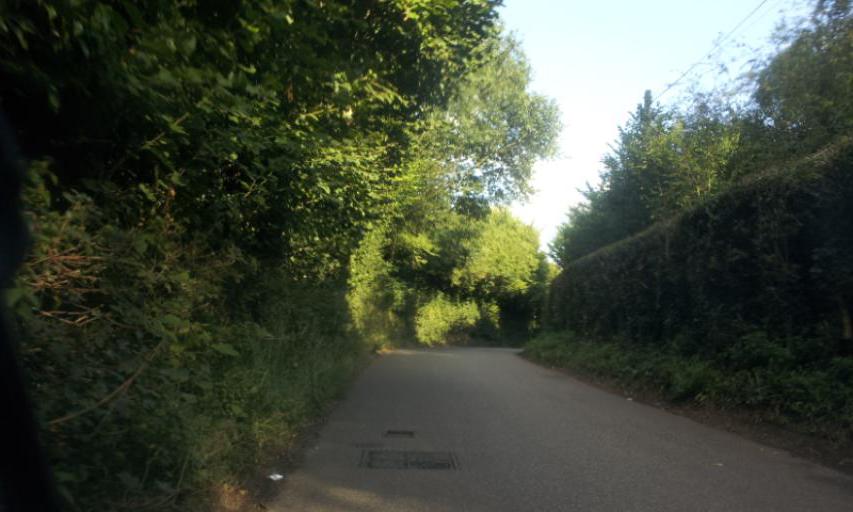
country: GB
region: England
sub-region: Kent
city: Swanley
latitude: 51.4059
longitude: 0.1783
